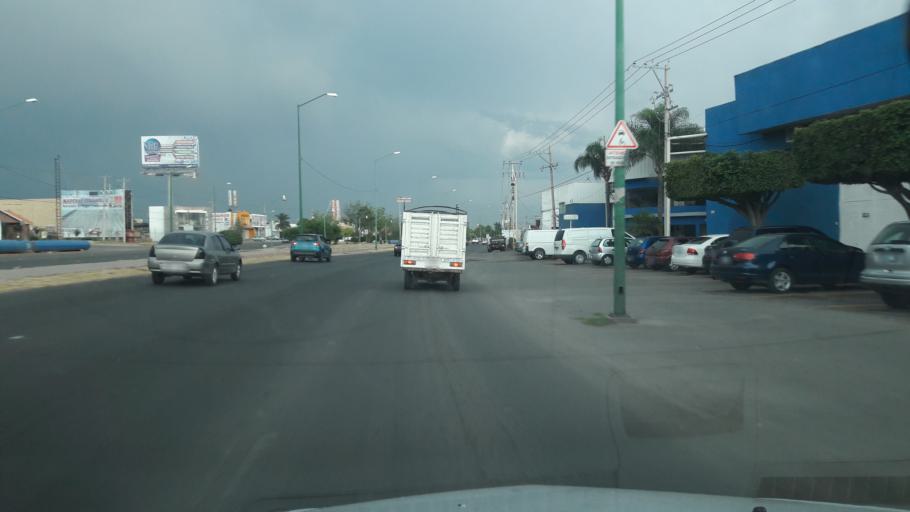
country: MX
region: Guanajuato
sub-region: Leon
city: Medina
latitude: 21.1512
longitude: -101.6358
